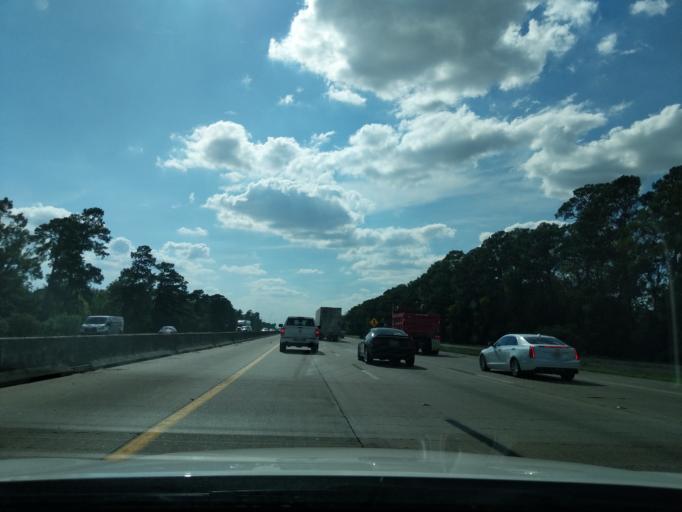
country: US
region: Texas
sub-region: Chambers County
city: Mont Belvieu
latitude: 29.8189
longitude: -94.9245
